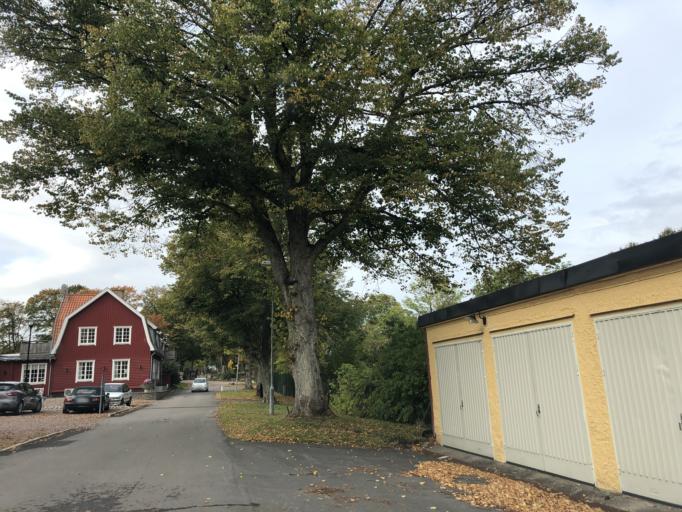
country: SE
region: Vaestra Goetaland
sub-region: Goteborg
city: Majorna
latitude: 57.6816
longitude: 11.8900
